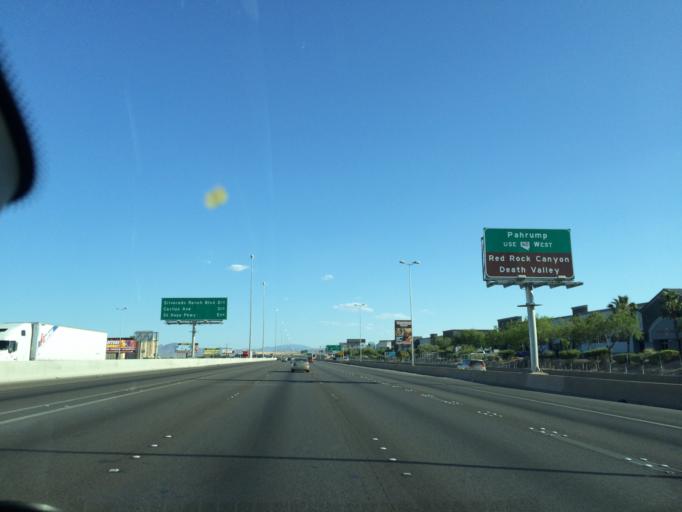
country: US
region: Nevada
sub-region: Clark County
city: Paradise
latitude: 36.0554
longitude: -115.1809
